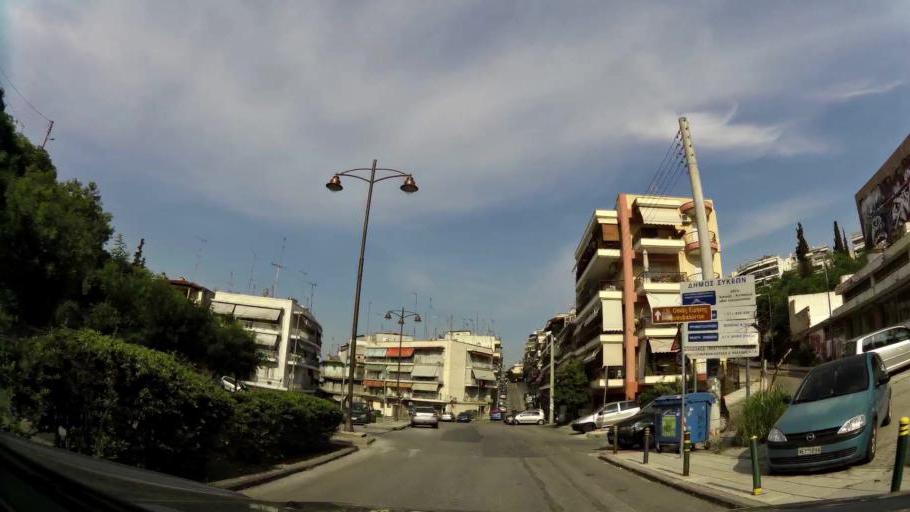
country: GR
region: Central Macedonia
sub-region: Nomos Thessalonikis
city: Sykies
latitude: 40.6454
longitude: 22.9446
